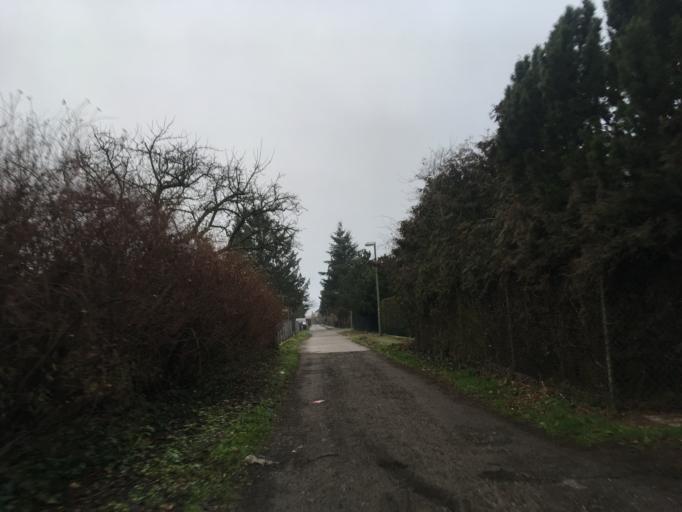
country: DE
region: Berlin
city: Buch
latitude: 52.6204
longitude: 13.4921
